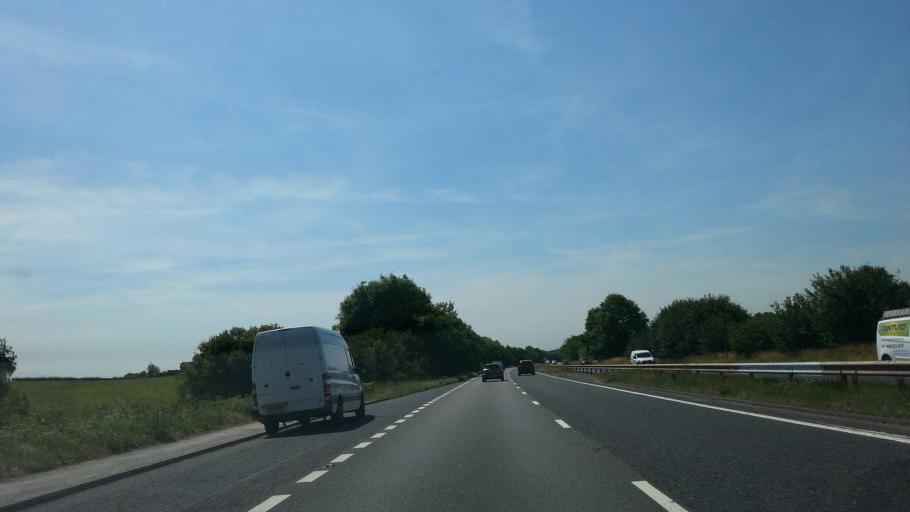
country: GB
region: England
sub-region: Derbyshire
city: Heage
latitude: 53.0452
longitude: -1.4280
